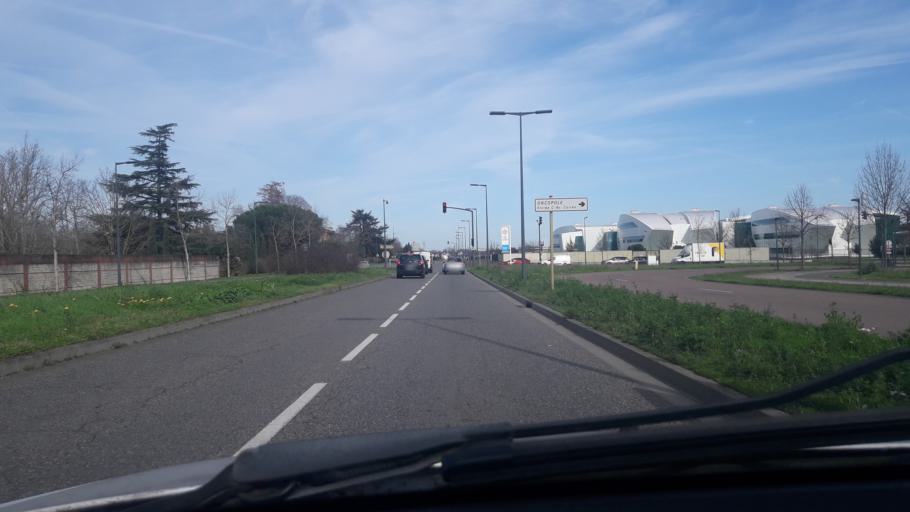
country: FR
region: Midi-Pyrenees
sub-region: Departement de la Haute-Garonne
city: Portet-sur-Garonne
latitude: 43.5570
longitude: 1.4240
